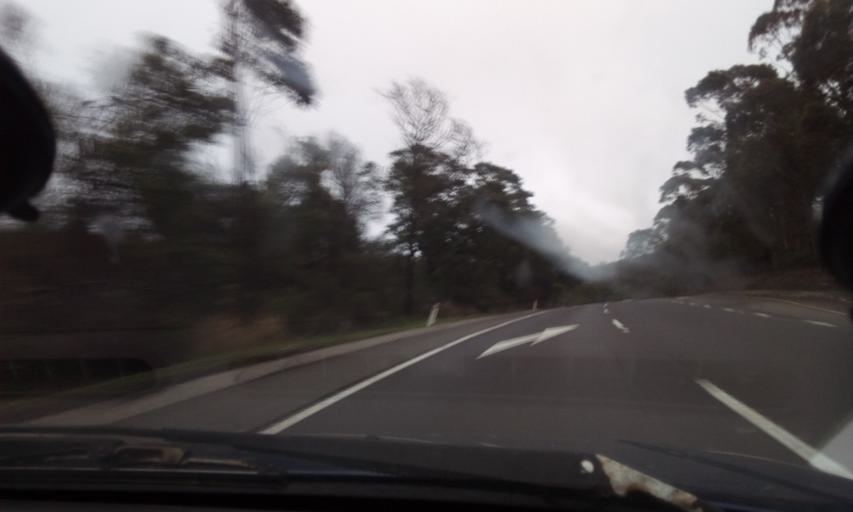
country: AU
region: New South Wales
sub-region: Wollongong
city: Mount Ousley
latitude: -34.3663
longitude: 150.8575
